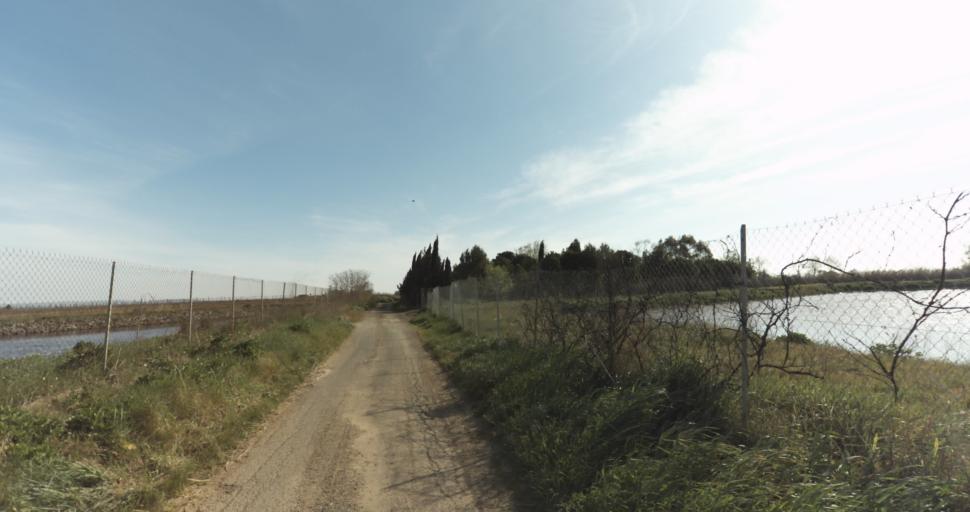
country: FR
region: Languedoc-Roussillon
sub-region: Departement de l'Herault
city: Marseillan
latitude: 43.3532
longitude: 3.5063
